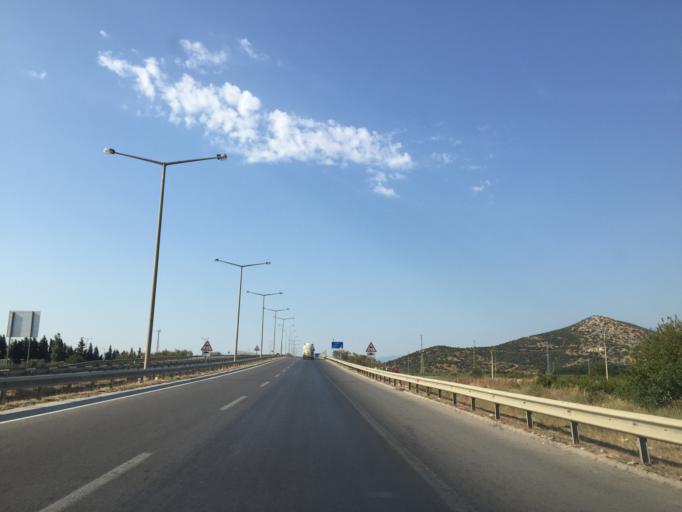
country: TR
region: Izmir
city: Belevi
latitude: 38.0224
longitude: 27.4416
